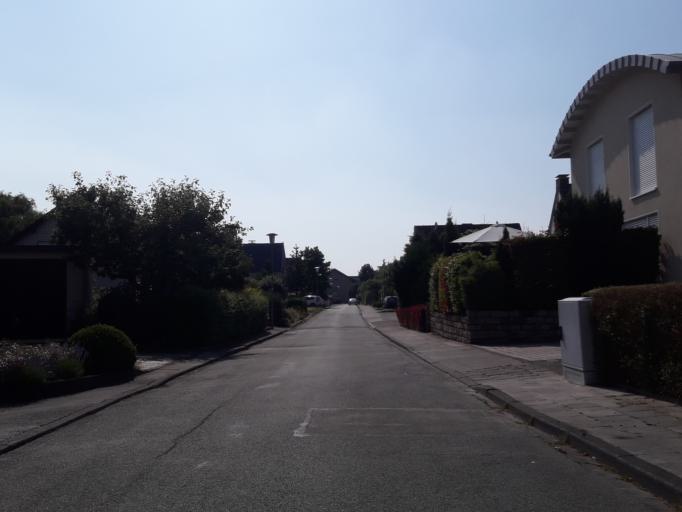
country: DE
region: North Rhine-Westphalia
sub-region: Regierungsbezirk Detmold
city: Paderborn
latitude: 51.6846
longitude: 8.6893
